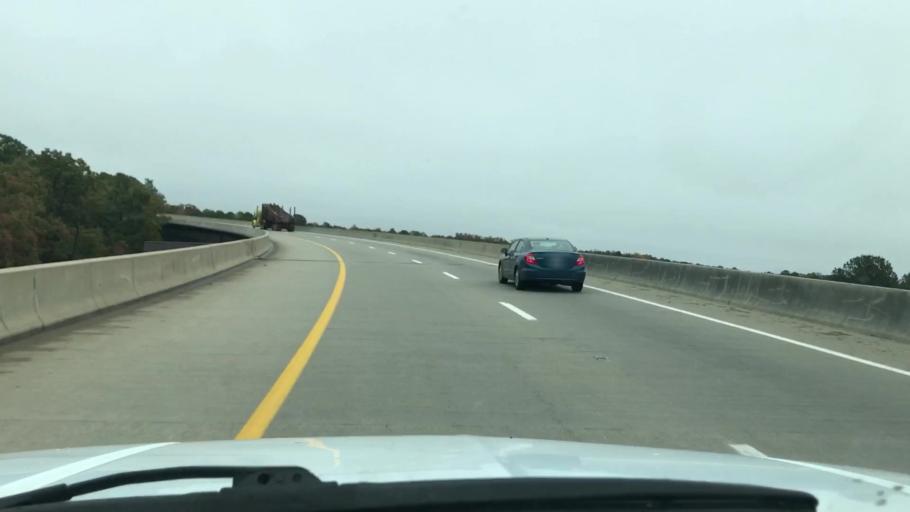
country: US
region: Virginia
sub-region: Henrico County
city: Short Pump
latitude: 37.6560
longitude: -77.6070
